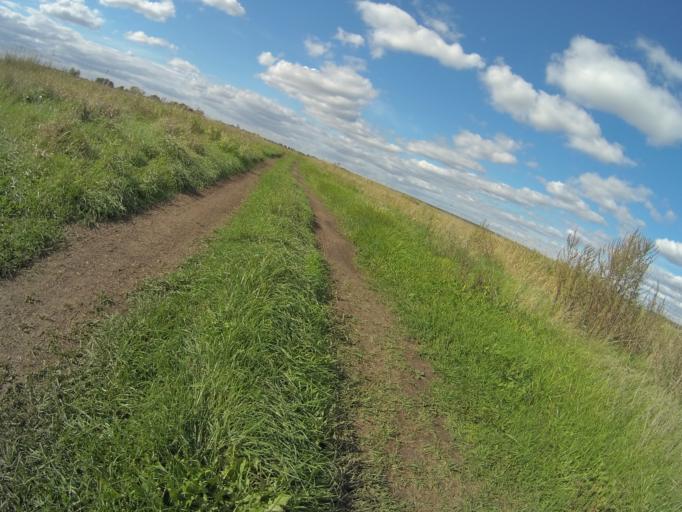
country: RU
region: Vladimir
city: Orgtrud
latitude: 56.3054
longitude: 40.6697
